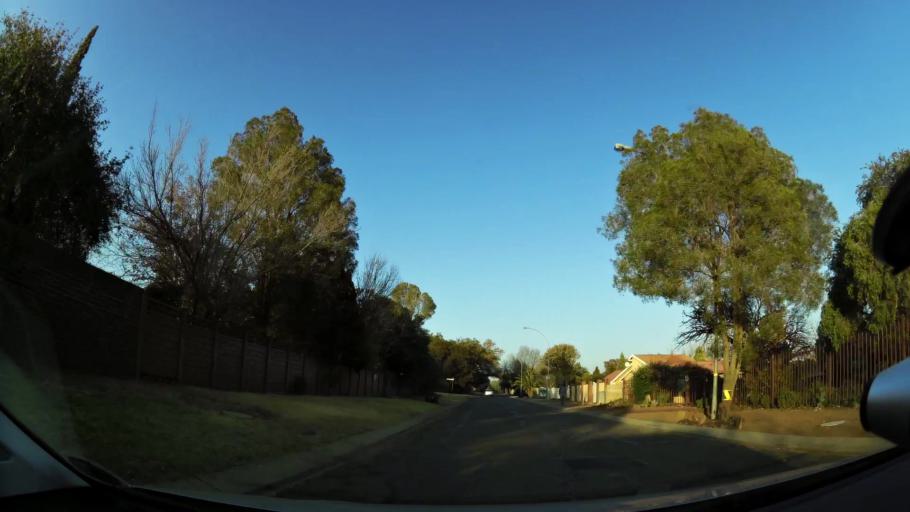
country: ZA
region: Orange Free State
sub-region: Mangaung Metropolitan Municipality
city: Bloemfontein
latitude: -29.0894
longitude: 26.1550
